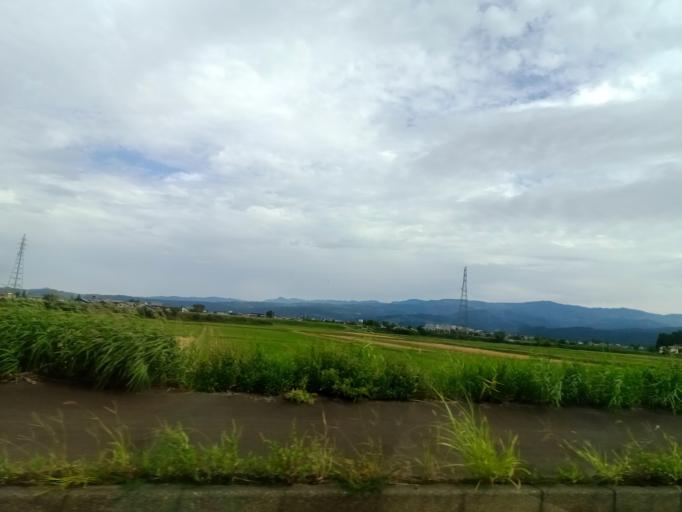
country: JP
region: Niigata
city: Arai
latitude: 37.0613
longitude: 138.2457
